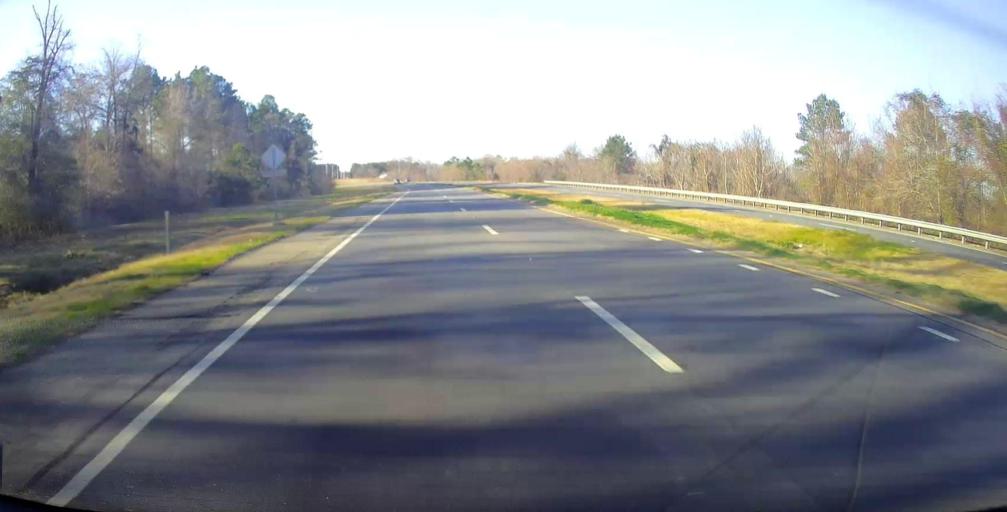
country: US
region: Georgia
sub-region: Lee County
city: Leesburg
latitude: 31.8095
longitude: -84.2089
